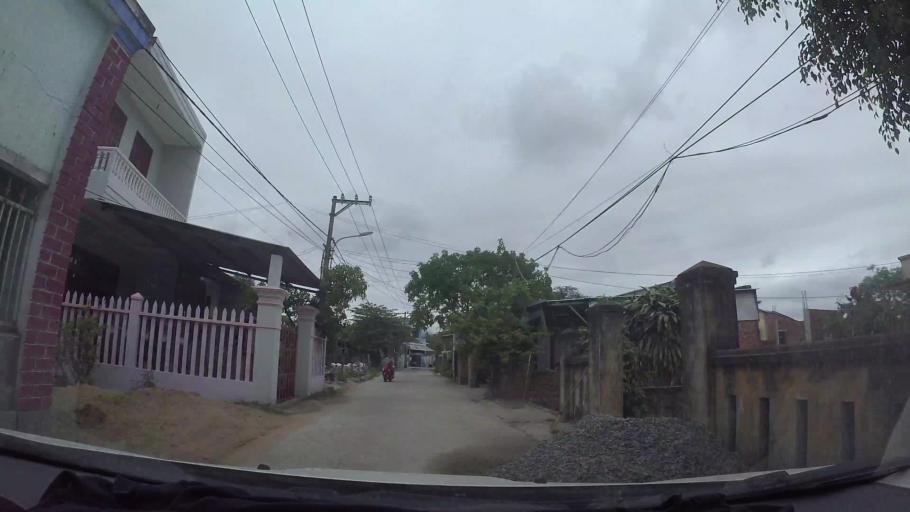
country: VN
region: Da Nang
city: Lien Chieu
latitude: 16.0862
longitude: 108.1026
